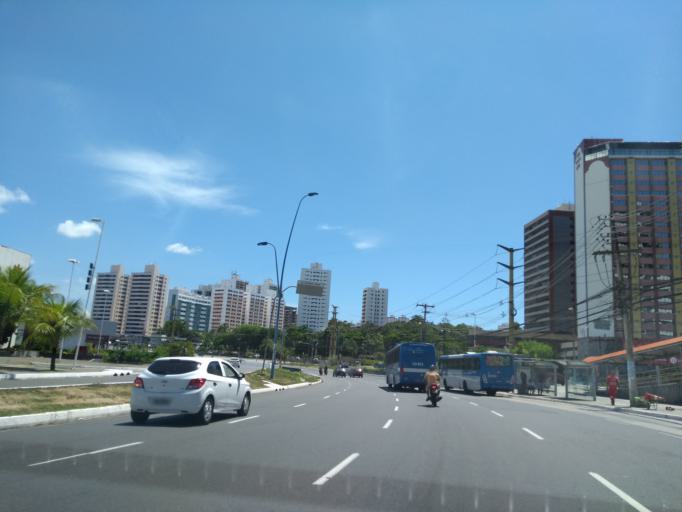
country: BR
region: Bahia
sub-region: Salvador
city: Salvador
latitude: -12.9841
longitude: -38.4522
